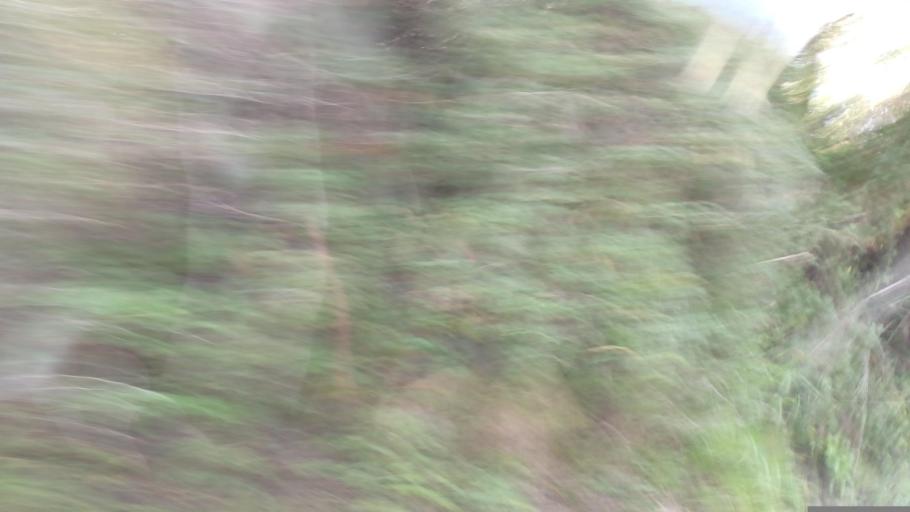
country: CY
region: Pafos
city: Mesogi
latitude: 34.8603
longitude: 32.5066
